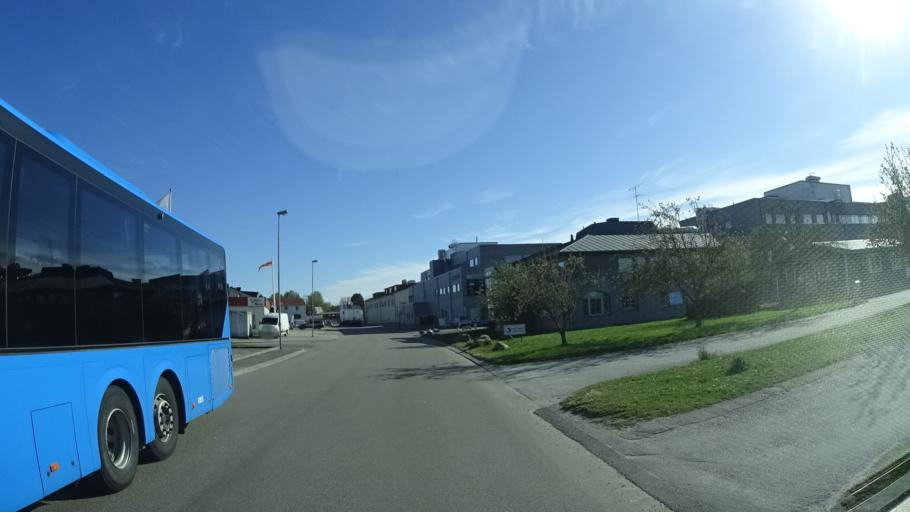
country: SE
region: Vaestra Goetaland
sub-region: Stenungsunds Kommun
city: Stenungsund
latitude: 58.0753
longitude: 11.8235
